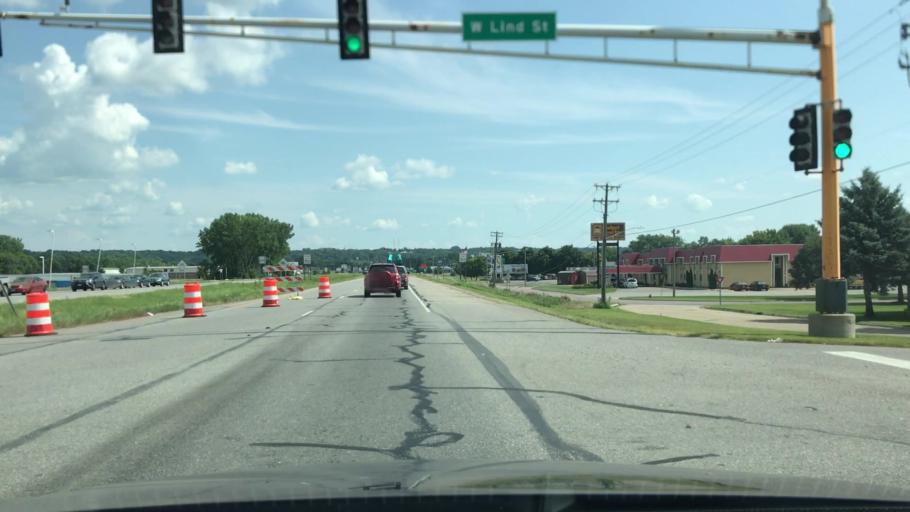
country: US
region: Minnesota
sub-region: Nicollet County
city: North Mankato
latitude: 44.1883
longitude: -94.0142
